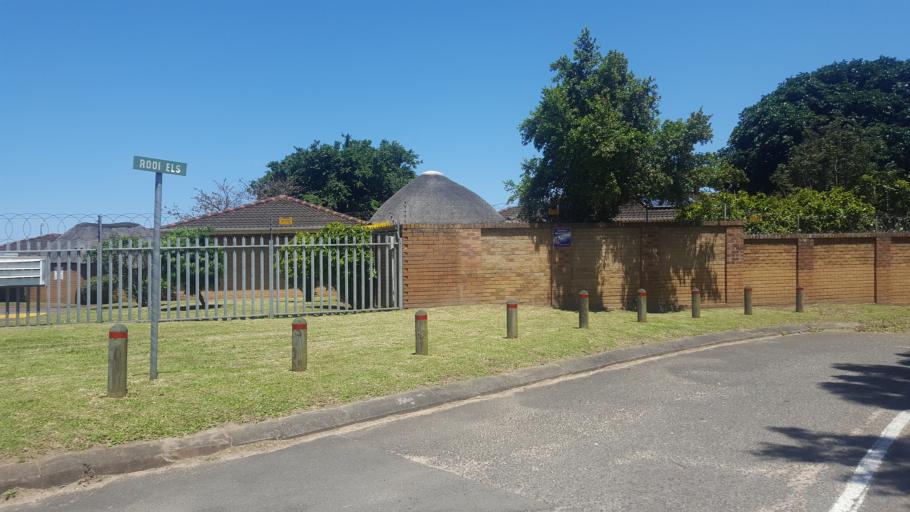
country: ZA
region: KwaZulu-Natal
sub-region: uThungulu District Municipality
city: Richards Bay
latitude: -28.7661
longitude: 32.0631
